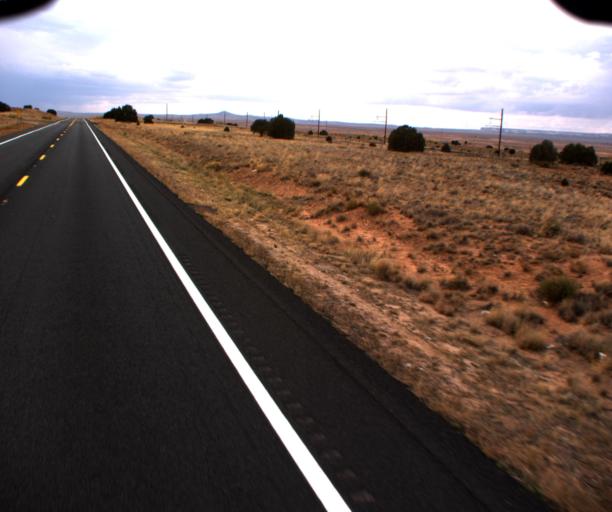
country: US
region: Arizona
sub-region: Coconino County
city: Kaibito
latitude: 36.4113
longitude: -110.8262
